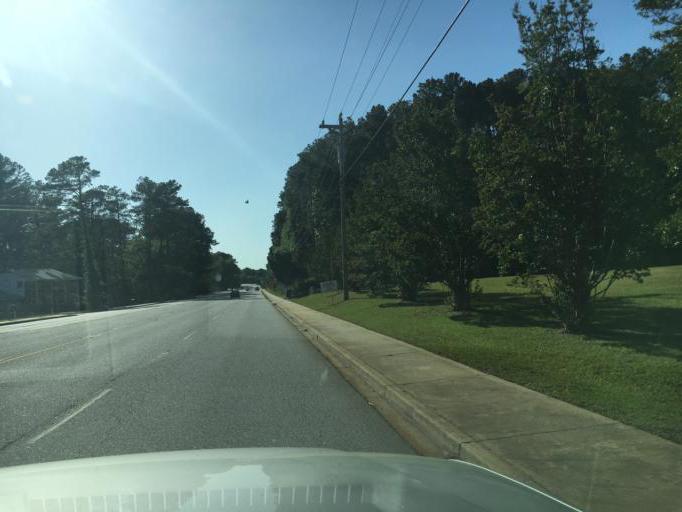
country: US
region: South Carolina
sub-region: Lexington County
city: Seven Oaks
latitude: 34.0447
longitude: -81.1431
